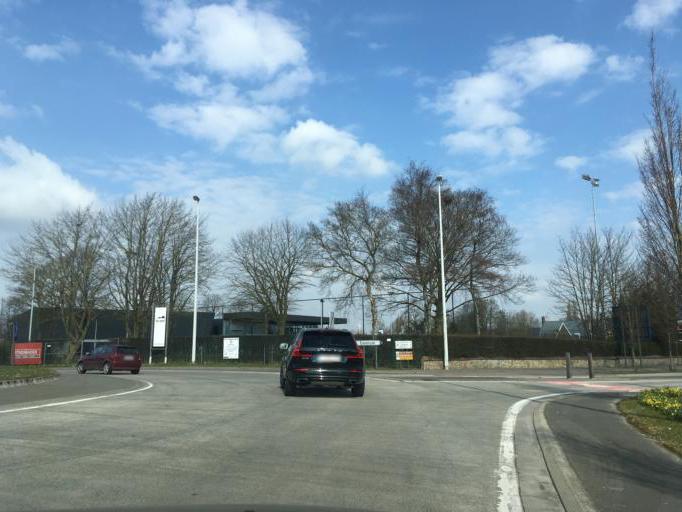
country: BE
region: Flanders
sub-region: Provincie West-Vlaanderen
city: Izegem
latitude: 50.9093
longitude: 3.2083
